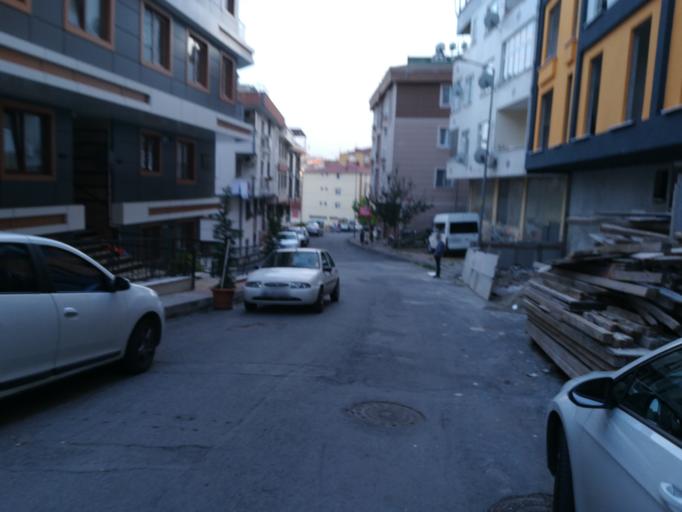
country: TR
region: Istanbul
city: Sisli
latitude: 41.0967
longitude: 28.9908
